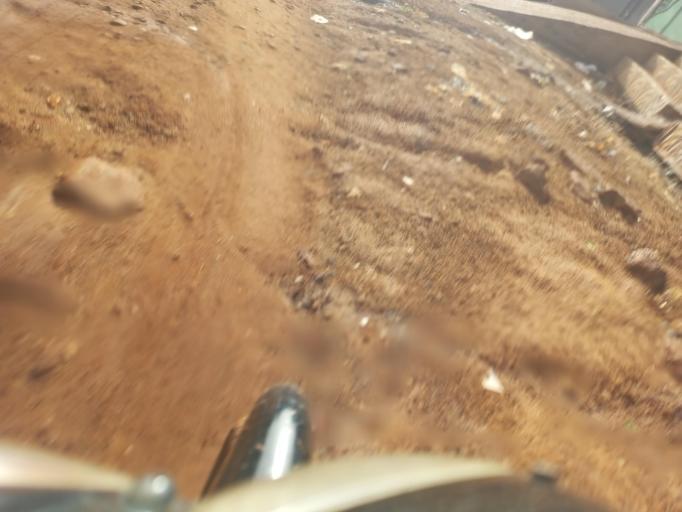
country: ML
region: Bamako
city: Bamako
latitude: 12.6002
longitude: -7.9868
